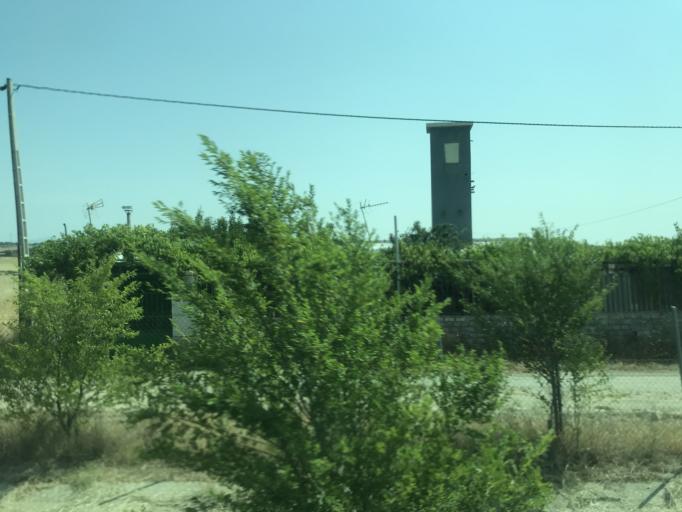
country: ES
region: Madrid
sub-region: Provincia de Madrid
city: Pedrezuela
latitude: 40.7583
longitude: -3.6000
